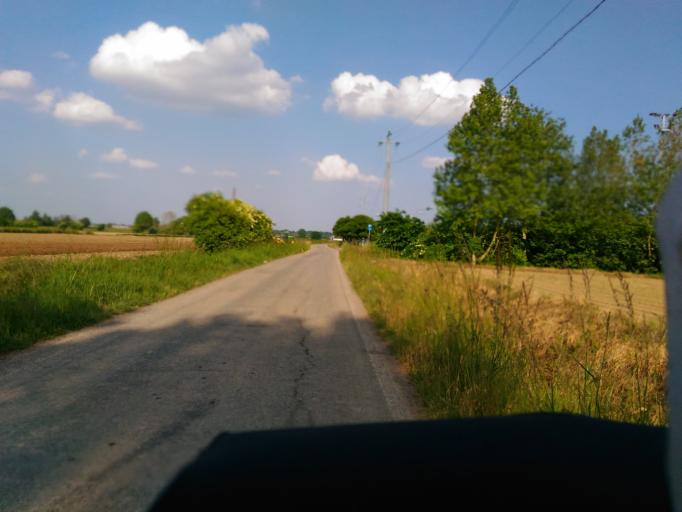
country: IT
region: Lombardy
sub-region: Citta metropolitana di Milano
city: Triginto
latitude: 45.4027
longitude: 9.3322
